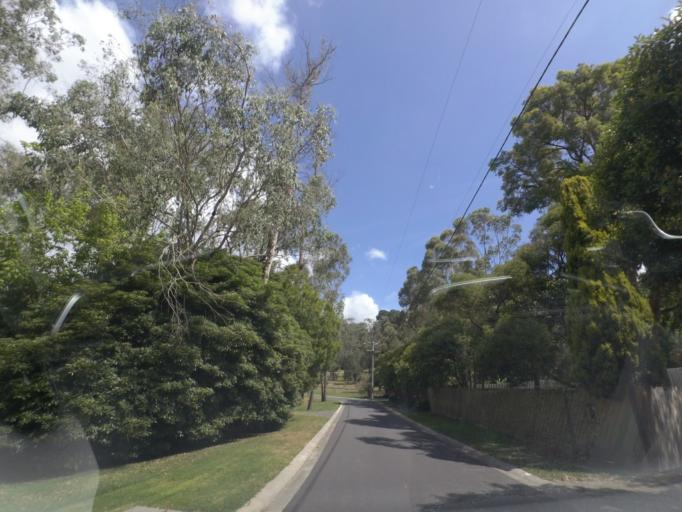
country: AU
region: Victoria
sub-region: Yarra Ranges
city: Mount Evelyn
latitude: -37.7826
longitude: 145.3587
